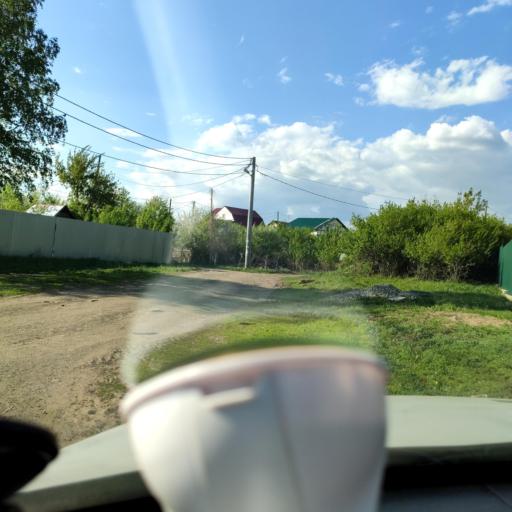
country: RU
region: Samara
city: Petra-Dubrava
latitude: 53.2593
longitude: 50.3445
